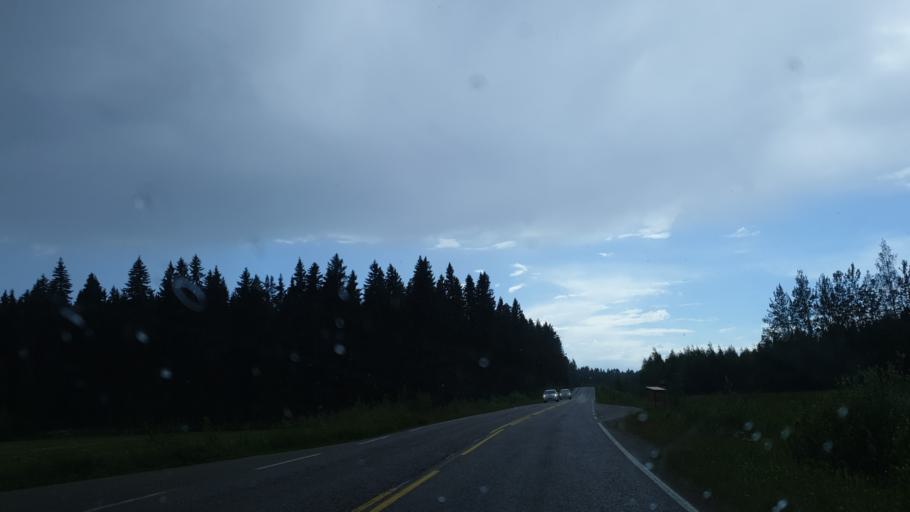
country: FI
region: Northern Savo
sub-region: Kuopio
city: Vehmersalmi
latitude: 62.9196
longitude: 27.9160
